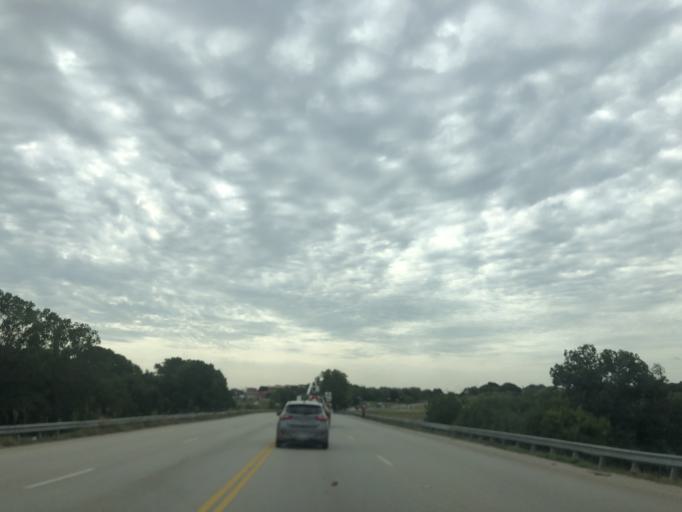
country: US
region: Texas
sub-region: Tarrant County
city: Richland Hills
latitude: 32.7805
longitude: -97.2198
